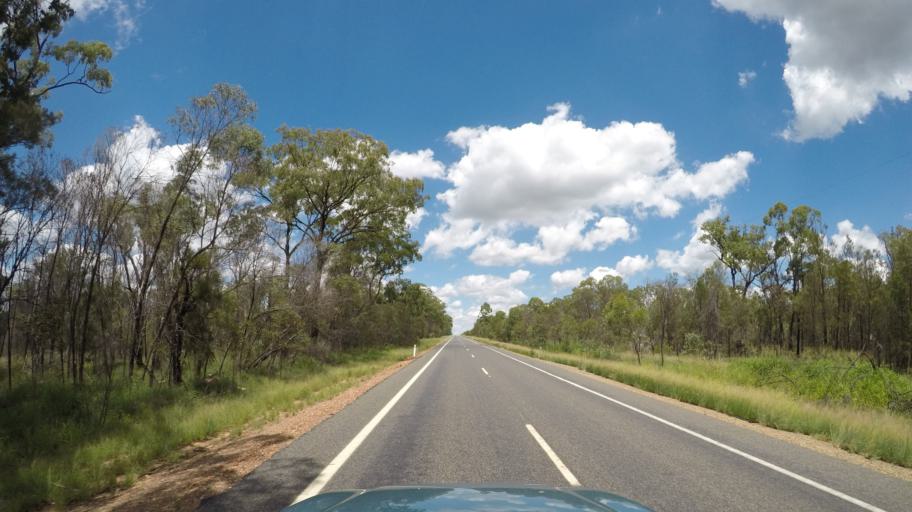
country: AU
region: Queensland
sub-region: Goondiwindi
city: Goondiwindi
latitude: -27.9979
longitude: 150.9445
